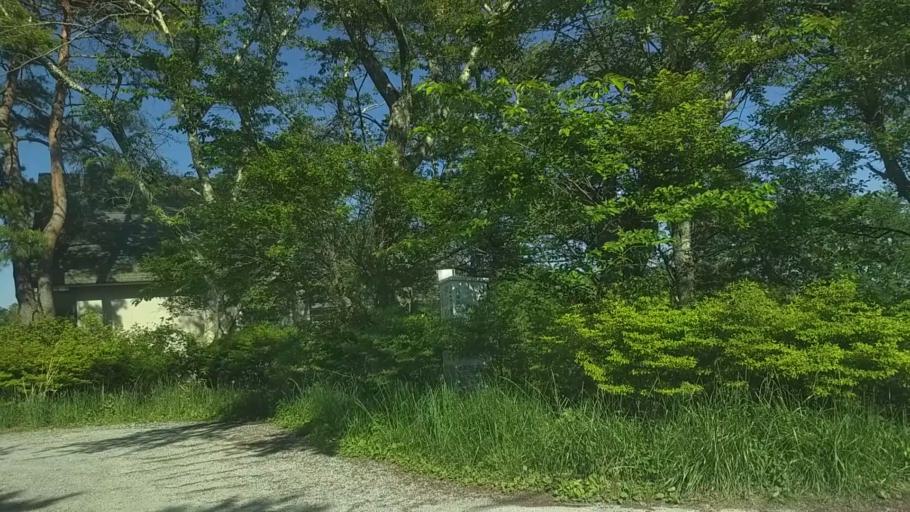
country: JP
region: Yamanashi
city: Nirasaki
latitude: 35.8795
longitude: 138.3597
